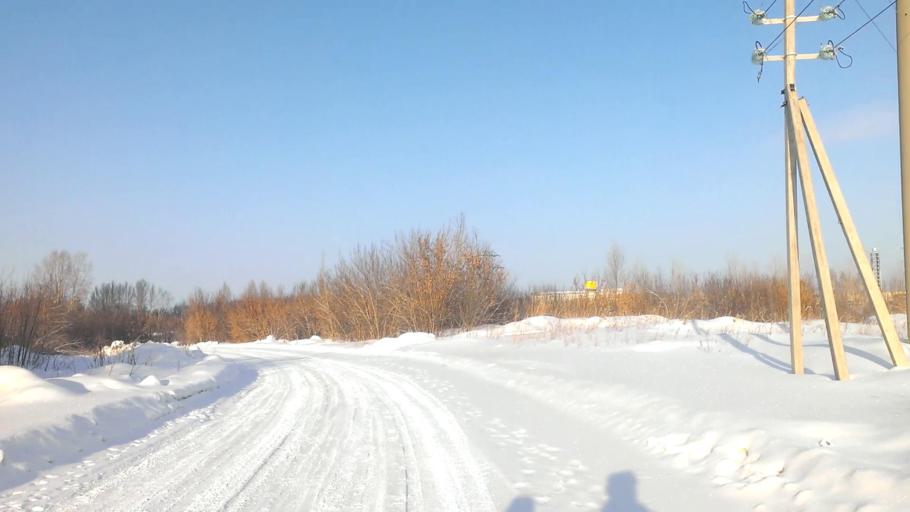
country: RU
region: Altai Krai
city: Novosilikatnyy
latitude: 53.3448
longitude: 83.6300
